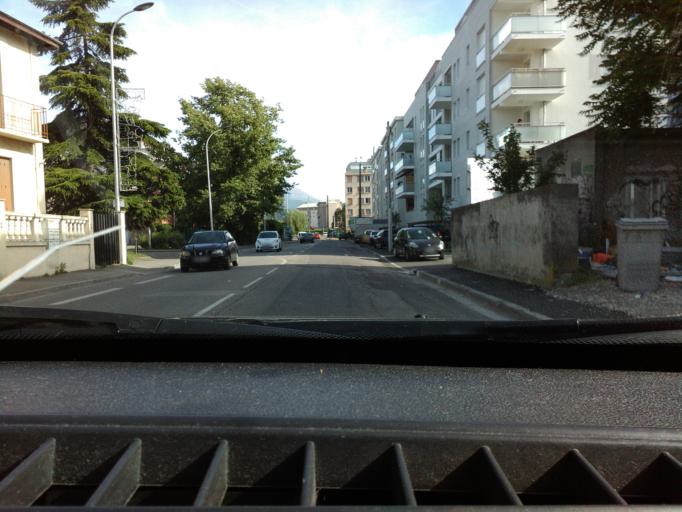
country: FR
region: Rhone-Alpes
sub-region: Departement de l'Isere
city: Saint-Martin-d'Heres
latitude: 45.1803
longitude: 5.7505
